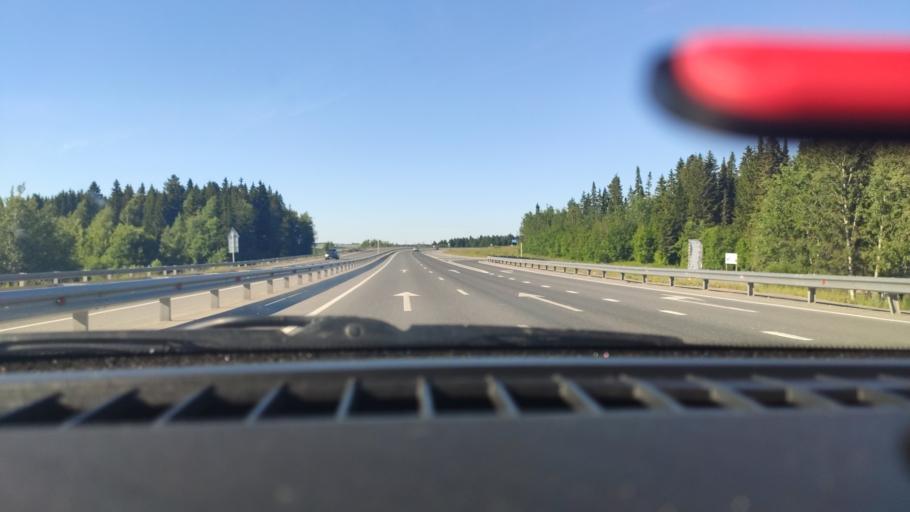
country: RU
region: Perm
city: Polazna
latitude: 58.2696
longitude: 56.4144
